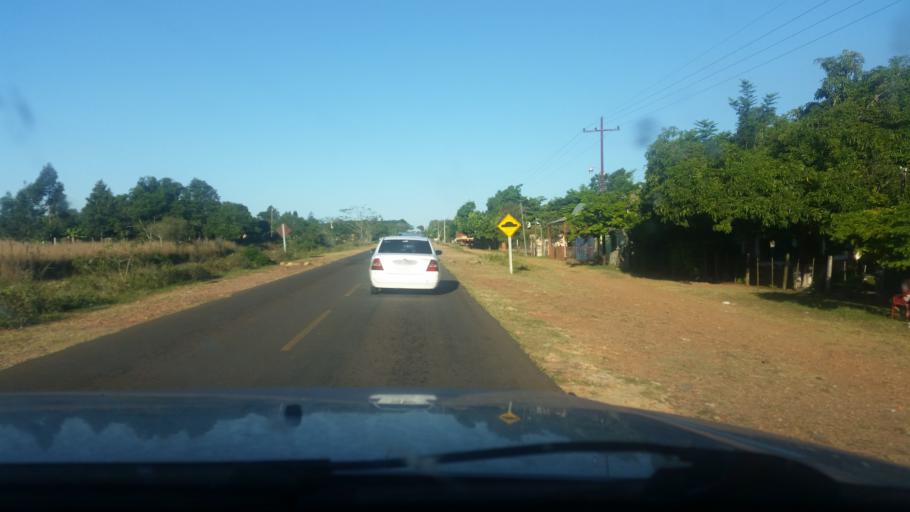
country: PY
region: Guaira
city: Independencia
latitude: -25.7224
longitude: -56.3240
